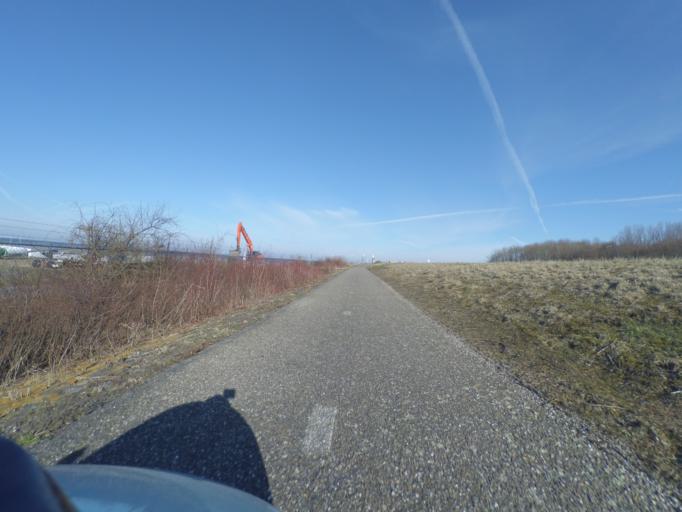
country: NL
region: North Holland
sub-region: Gemeente Naarden
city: Naarden
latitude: 52.3466
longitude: 5.1345
